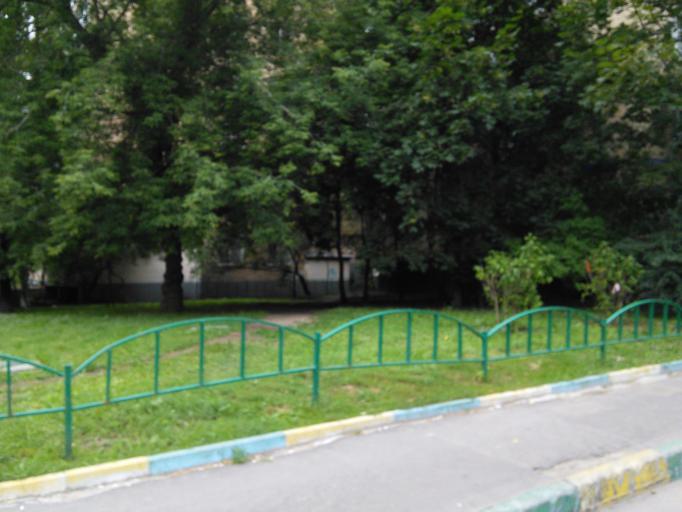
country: RU
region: Moscow
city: Luzhniki
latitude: 55.7244
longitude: 37.5734
